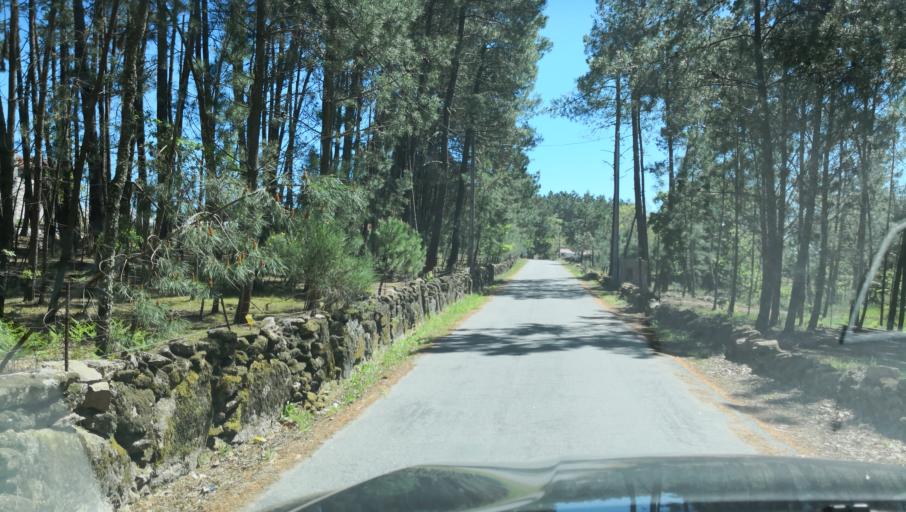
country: PT
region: Vila Real
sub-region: Vila Real
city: Vila Real
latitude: 41.2951
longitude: -7.6587
